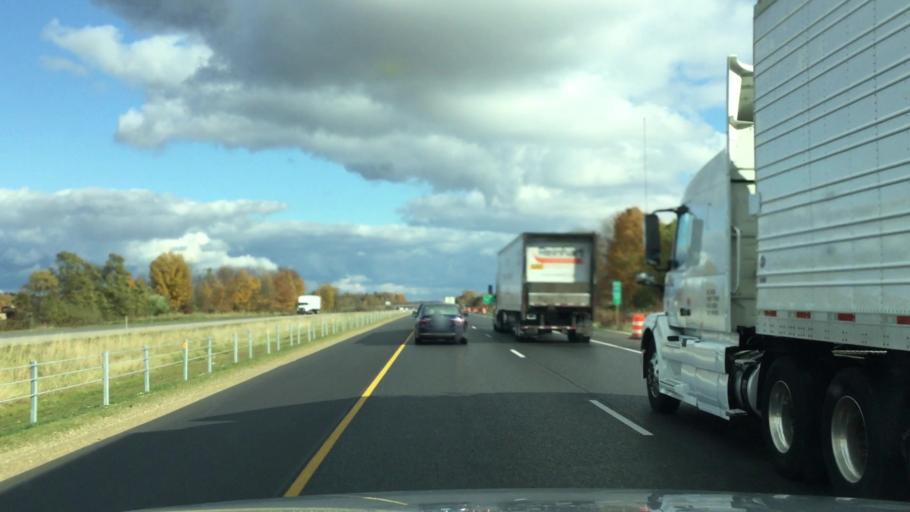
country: US
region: Michigan
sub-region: Van Buren County
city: Hartford
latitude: 42.1971
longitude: -86.0819
